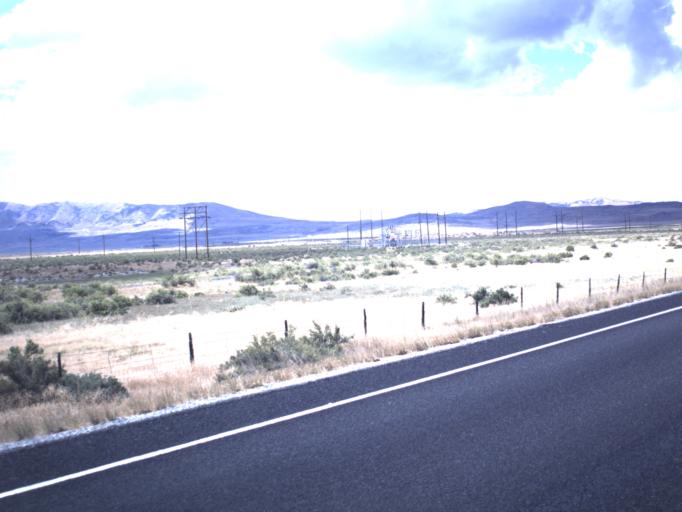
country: US
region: Utah
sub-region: Box Elder County
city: Tremonton
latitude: 41.6187
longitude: -112.3836
